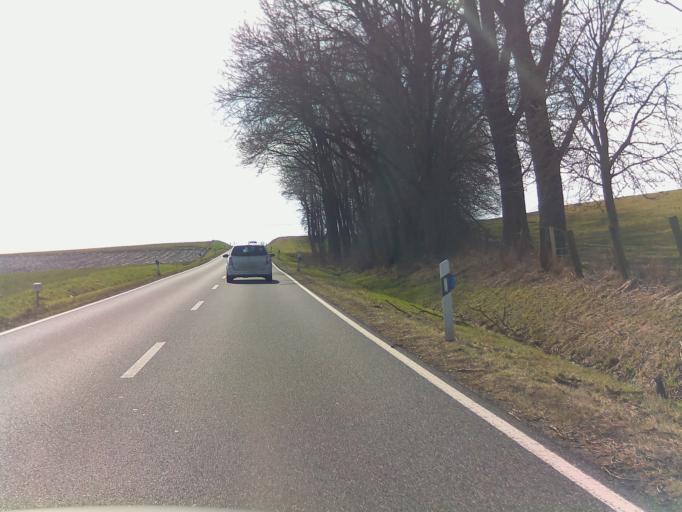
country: DE
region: Hesse
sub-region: Regierungsbezirk Giessen
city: Grunberg
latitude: 50.6129
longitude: 8.9491
